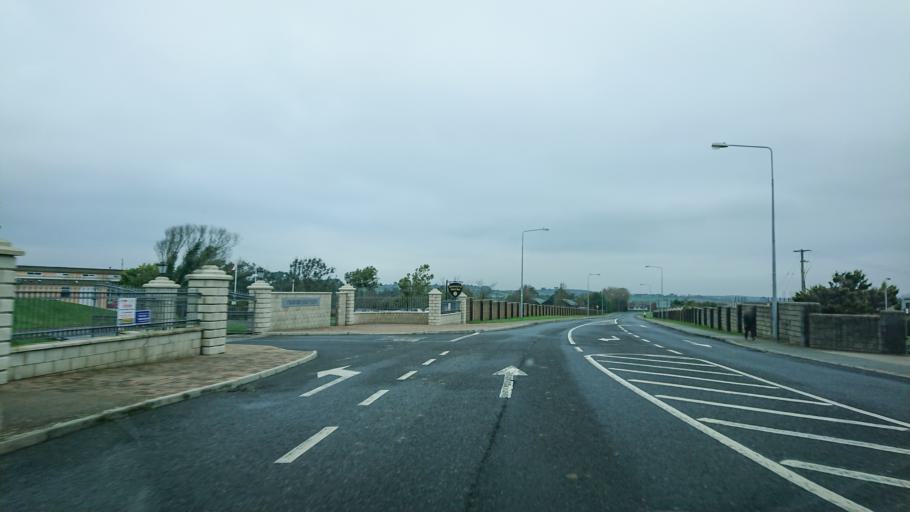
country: IE
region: Munster
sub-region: Waterford
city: Tra Mhor
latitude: 52.1552
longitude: -7.1698
